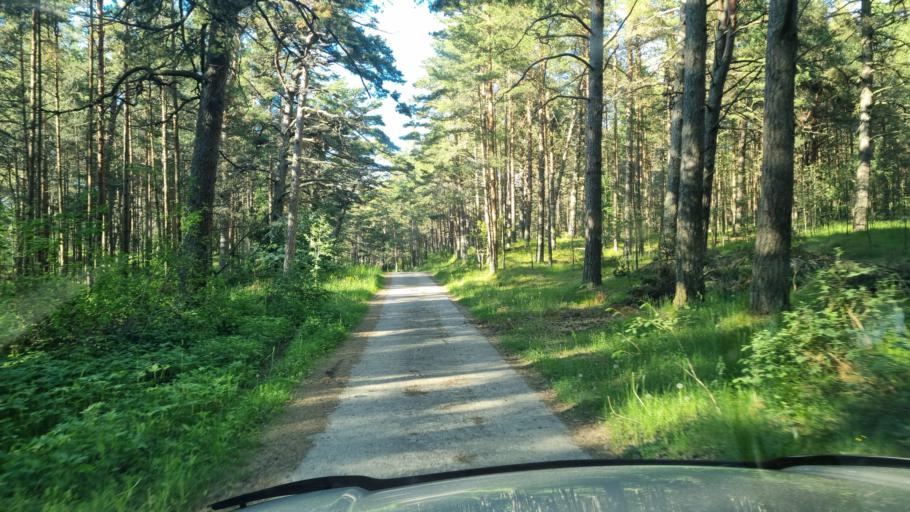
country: LV
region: Ventspils
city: Ventspils
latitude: 57.3684
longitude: 21.5192
